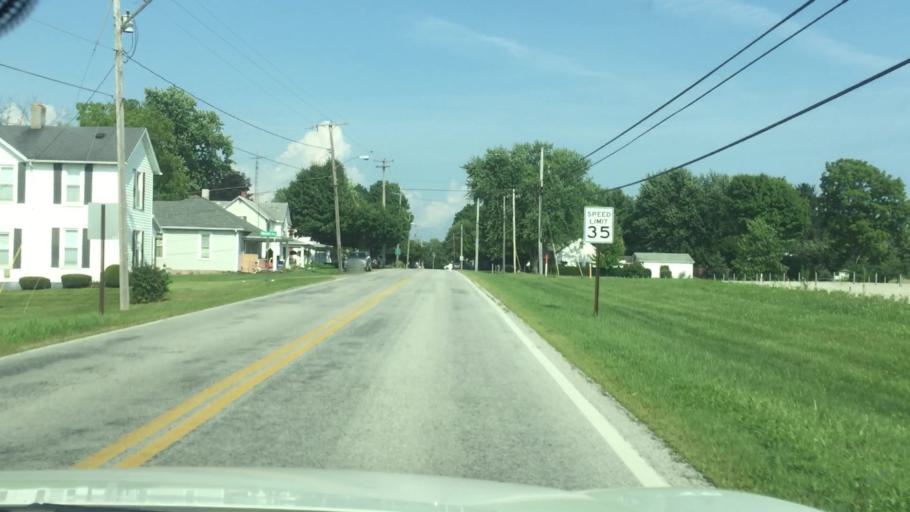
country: US
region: Ohio
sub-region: Clark County
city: Northridge
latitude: 39.9924
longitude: -83.7211
